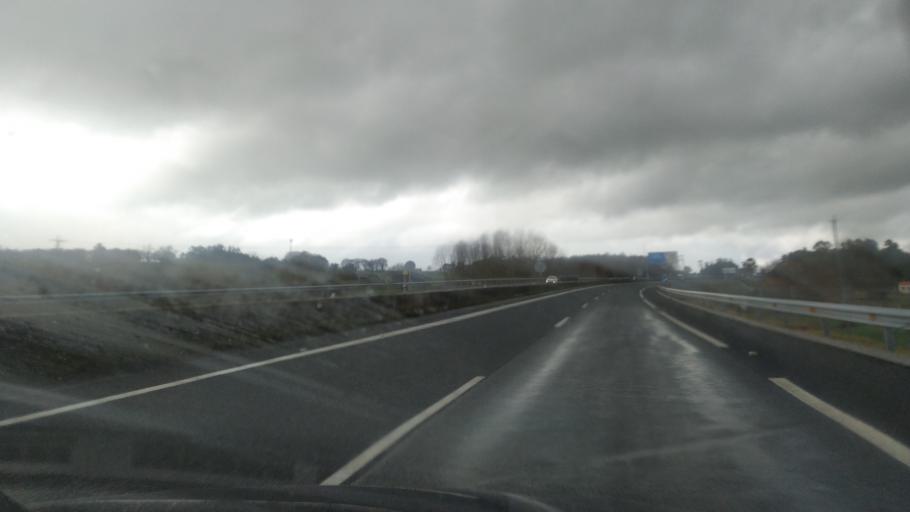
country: ES
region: Galicia
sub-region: Provincia de Pontevedra
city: Silleda
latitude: 42.7111
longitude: -8.2335
